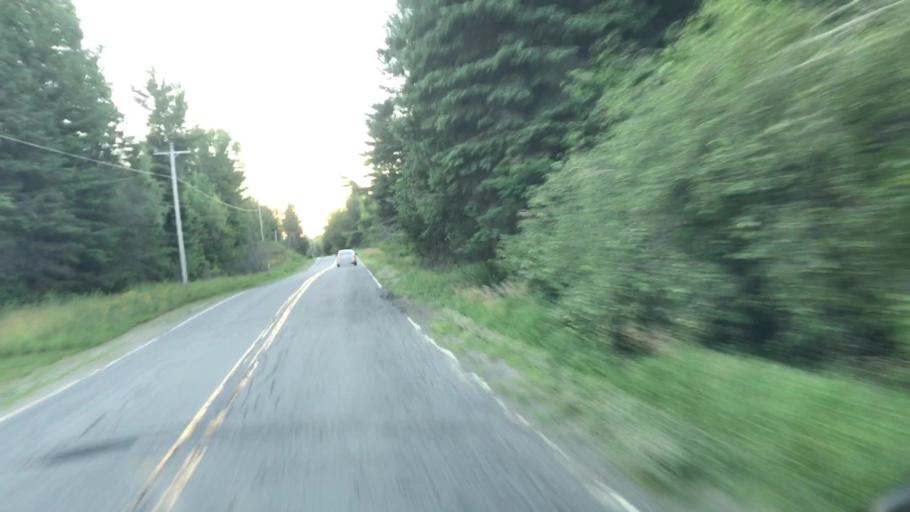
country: US
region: Maine
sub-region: Penobscot County
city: Medway
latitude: 45.6075
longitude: -68.2563
